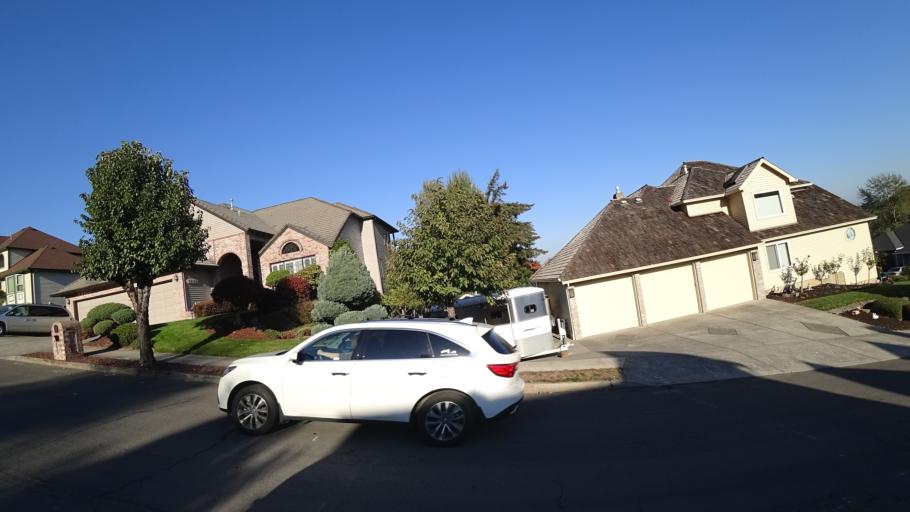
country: US
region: Oregon
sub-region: Multnomah County
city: Gresham
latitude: 45.4858
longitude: -122.4276
